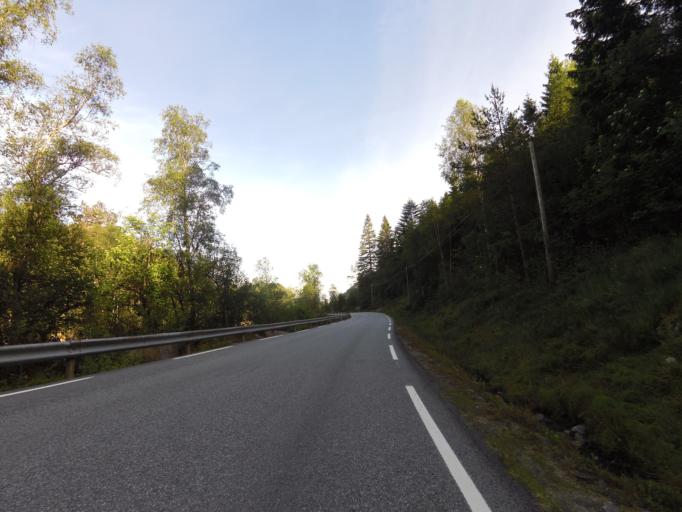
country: NO
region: Vest-Agder
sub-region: Flekkefjord
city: Flekkefjord
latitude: 58.2810
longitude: 6.6233
